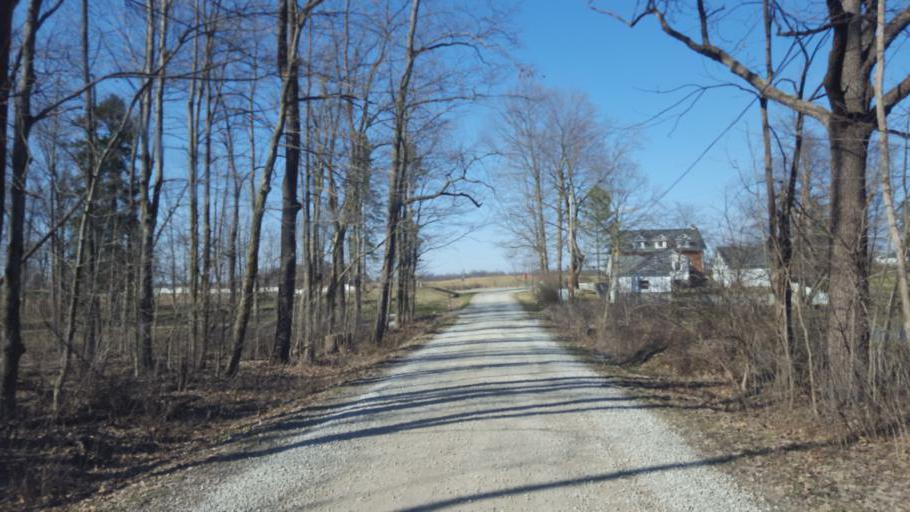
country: US
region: Ohio
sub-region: Morrow County
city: Mount Gilead
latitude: 40.5375
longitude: -82.7780
